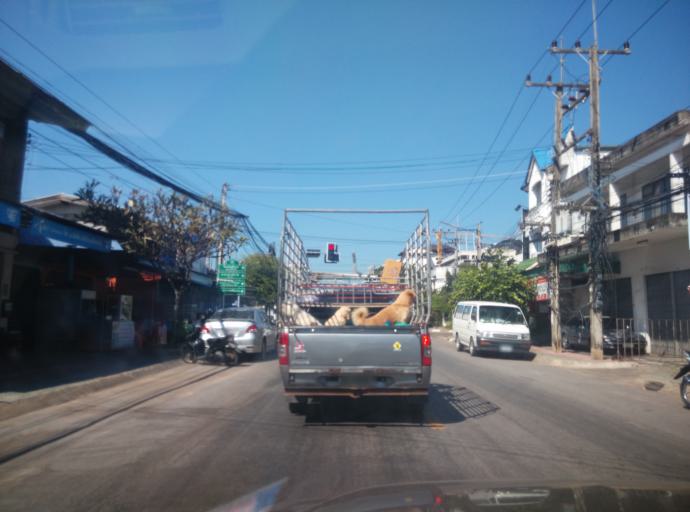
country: TH
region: Sisaket
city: Si Sa Ket
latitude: 15.1145
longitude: 104.3232
